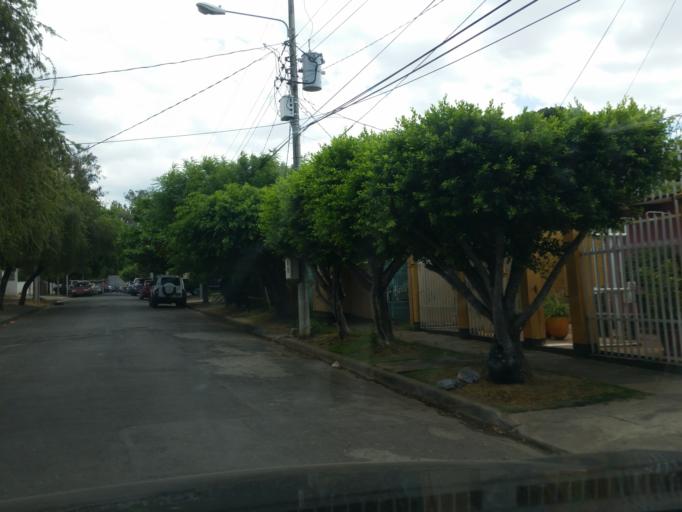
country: NI
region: Managua
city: Managua
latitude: 12.1256
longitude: -86.2637
